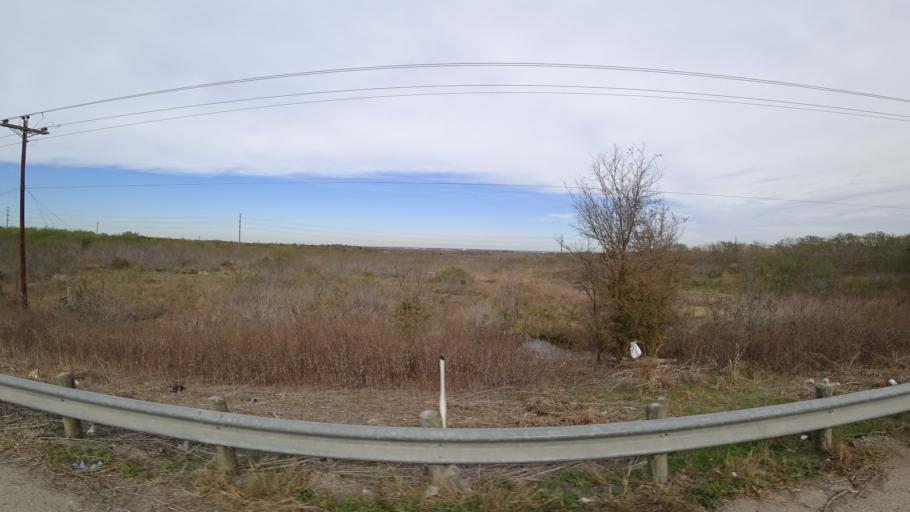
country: US
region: Texas
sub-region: Travis County
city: Garfield
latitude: 30.1500
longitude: -97.5827
